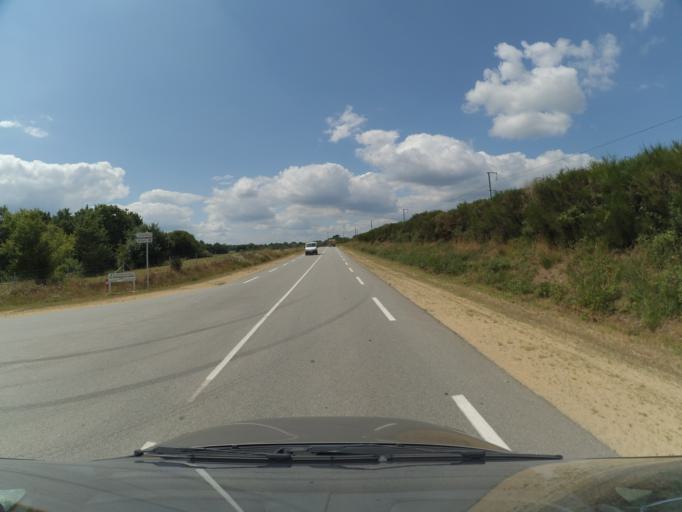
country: FR
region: Brittany
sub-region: Departement du Morbihan
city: Landevant
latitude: 47.7568
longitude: -3.1133
